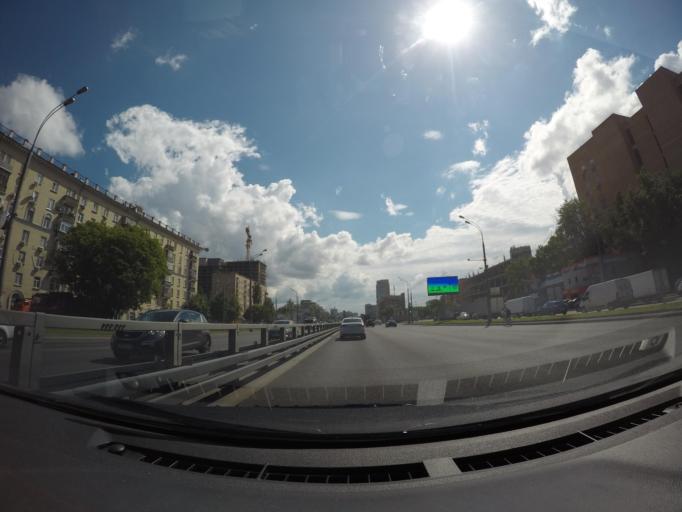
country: RU
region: Moscow
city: Ryazanskiy
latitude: 55.7235
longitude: 37.7680
